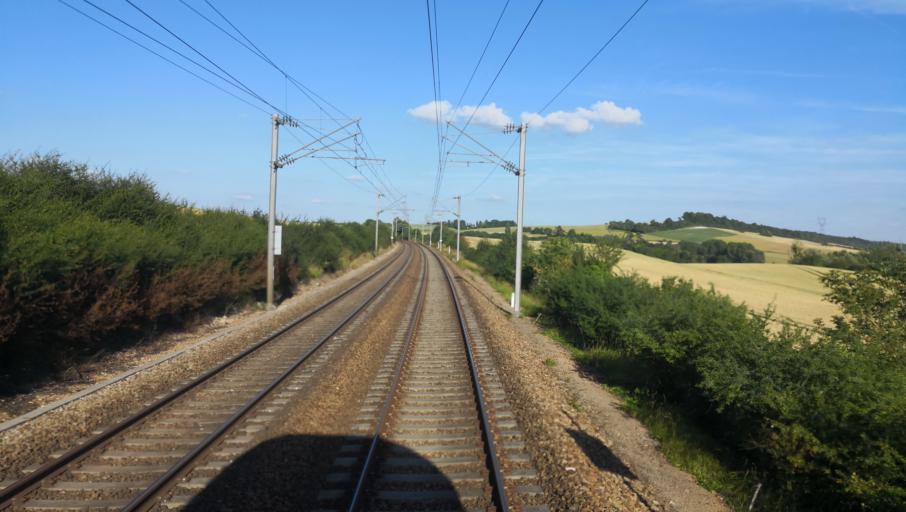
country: FR
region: Haute-Normandie
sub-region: Departement de l'Eure
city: Bueil
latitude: 48.9203
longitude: 1.4547
